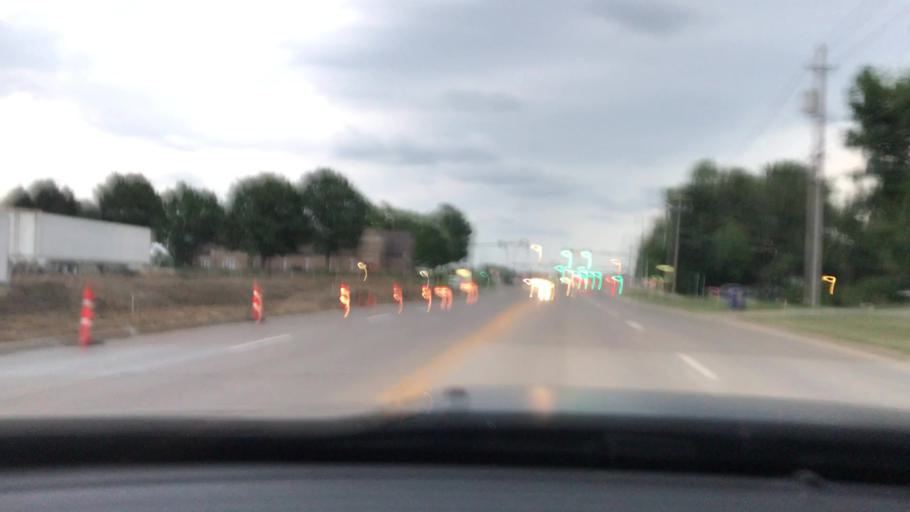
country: US
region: Iowa
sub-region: Scott County
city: Bettendorf
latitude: 41.5748
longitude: -90.5340
